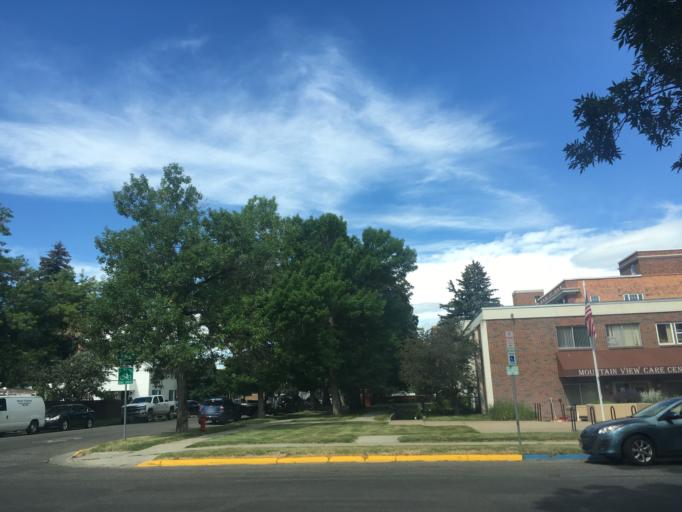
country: US
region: Montana
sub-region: Gallatin County
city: Bozeman
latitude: 45.6815
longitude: -111.0370
